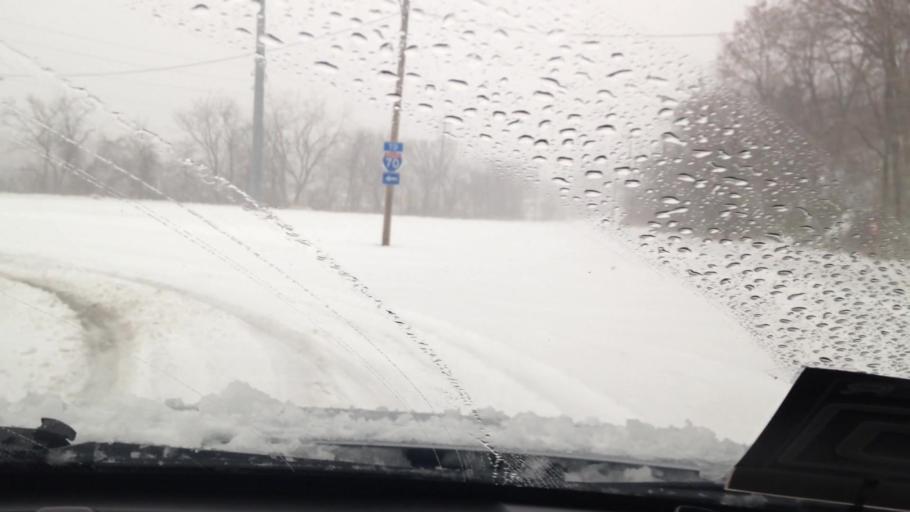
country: US
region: Missouri
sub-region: Jackson County
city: Sugar Creek
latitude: 39.0692
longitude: -94.4983
